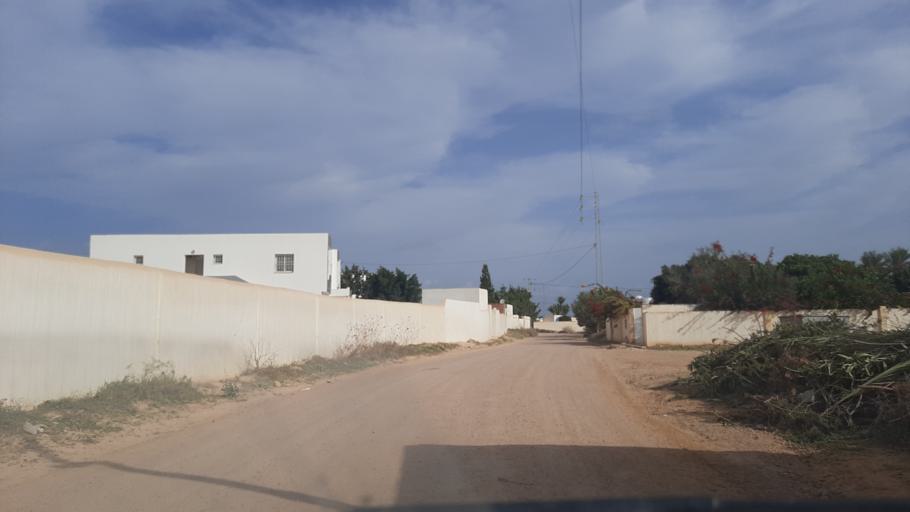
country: TN
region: Madanin
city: Midoun
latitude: 33.8163
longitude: 11.0254
